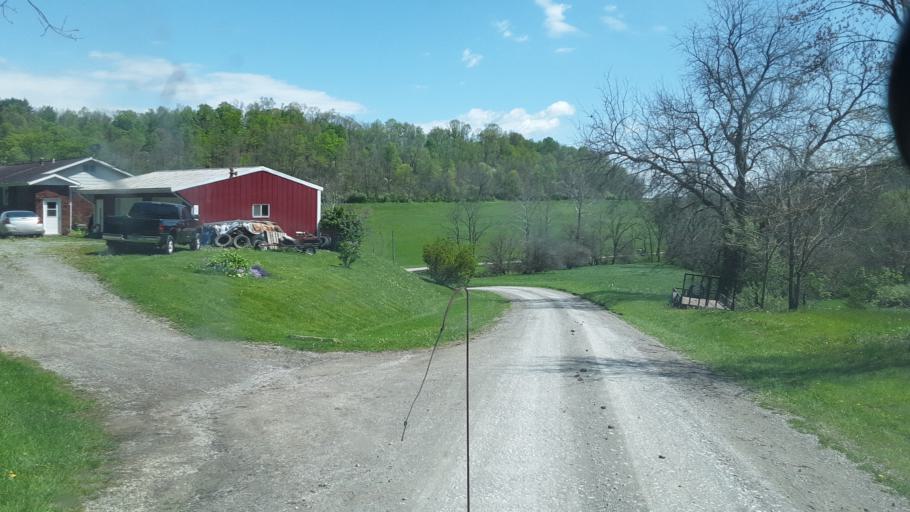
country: US
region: Ohio
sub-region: Noble County
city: Caldwell
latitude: 39.7703
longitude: -81.6005
